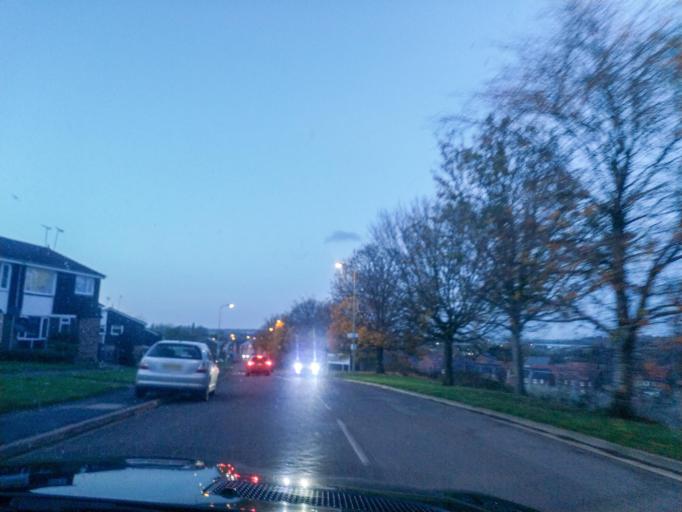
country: GB
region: England
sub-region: Oxfordshire
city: Banbury
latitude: 52.0481
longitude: -1.3217
